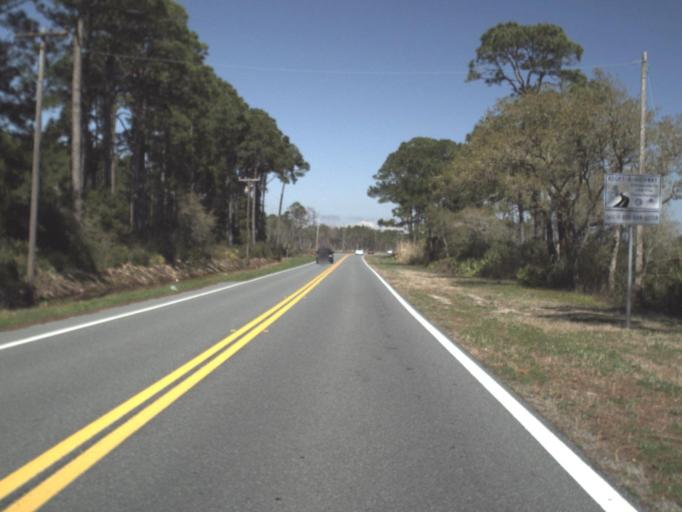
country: US
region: Florida
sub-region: Franklin County
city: Carrabelle
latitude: 29.8578
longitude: -84.6312
